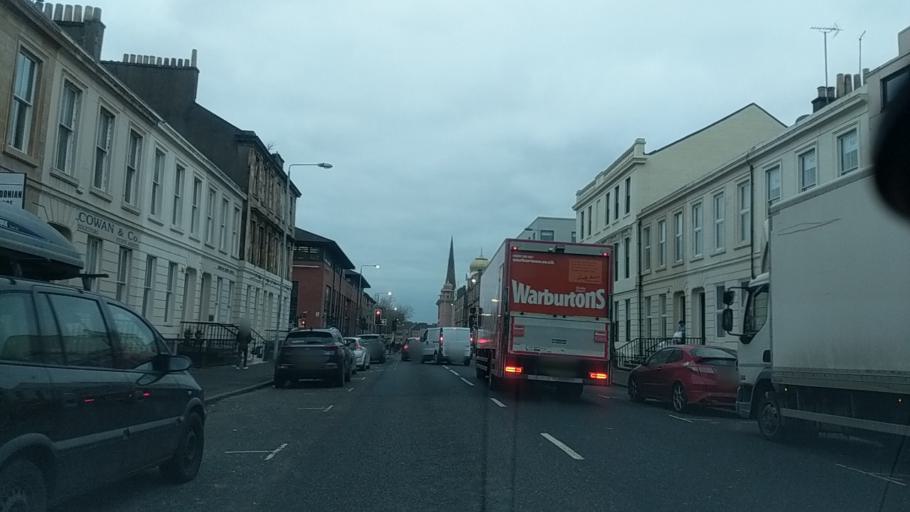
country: GB
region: Scotland
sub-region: Glasgow City
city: Glasgow
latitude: 55.8652
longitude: -4.2750
